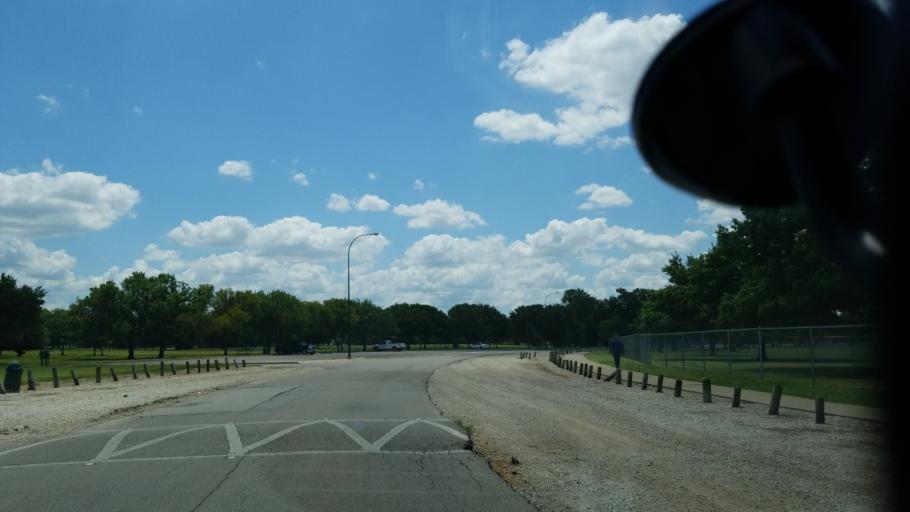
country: US
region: Texas
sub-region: Dallas County
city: Cockrell Hill
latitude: 32.7124
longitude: -96.8510
